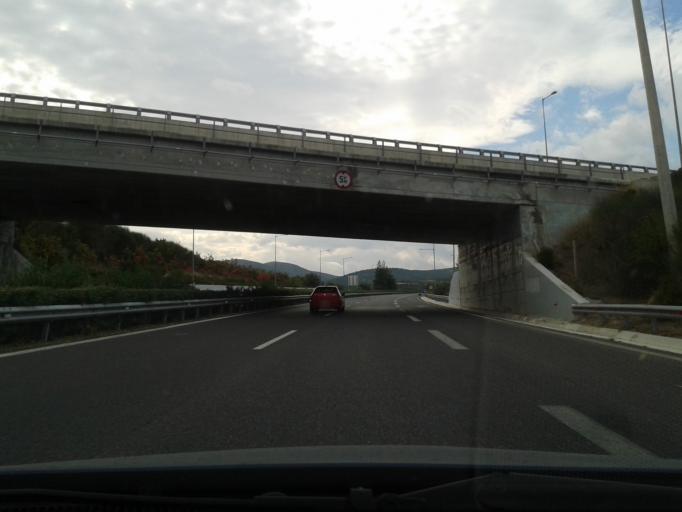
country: GR
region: Peloponnese
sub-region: Nomos Korinthias
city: Ayios Vasilios
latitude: 37.8133
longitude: 22.7787
